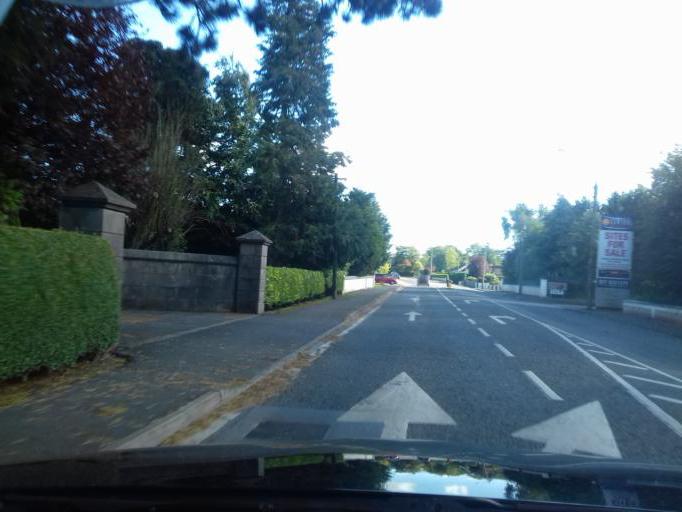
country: IE
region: Leinster
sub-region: Uibh Fhaili
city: Tullamore
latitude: 53.2610
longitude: -7.4847
